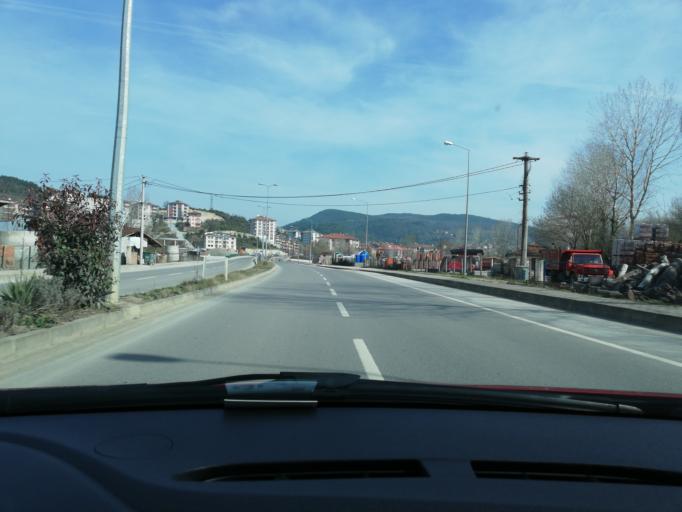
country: TR
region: Bartin
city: Bartin
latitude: 41.6398
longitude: 32.3544
